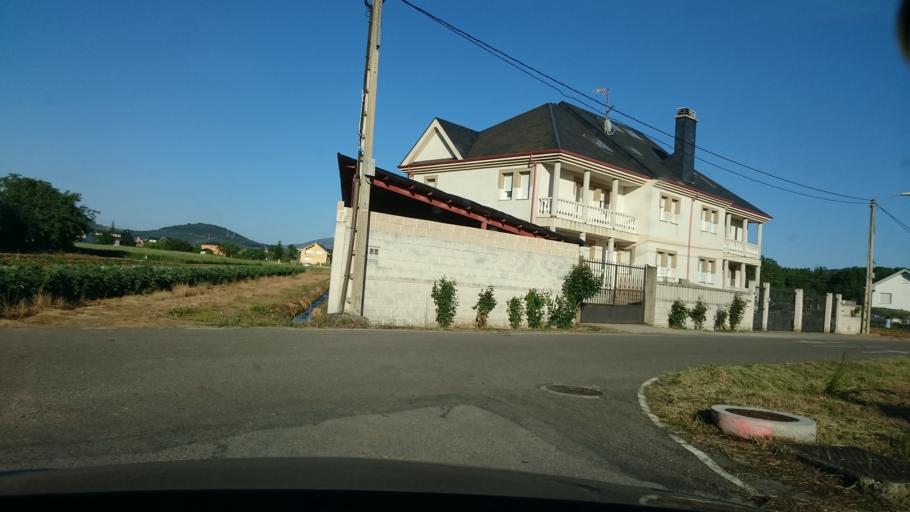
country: ES
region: Castille and Leon
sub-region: Provincia de Leon
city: Camponaraya
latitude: 42.5677
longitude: -6.6562
